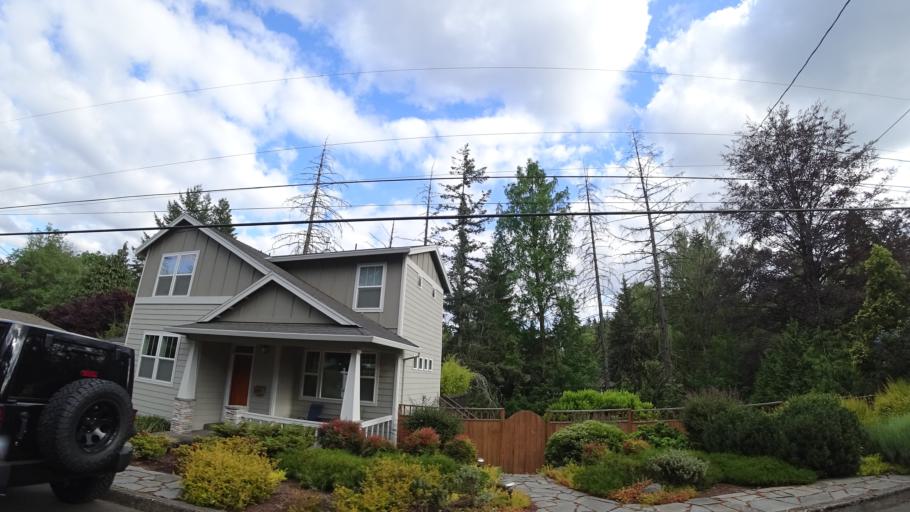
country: US
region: Oregon
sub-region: Washington County
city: Garden Home-Whitford
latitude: 45.4772
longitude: -122.7340
